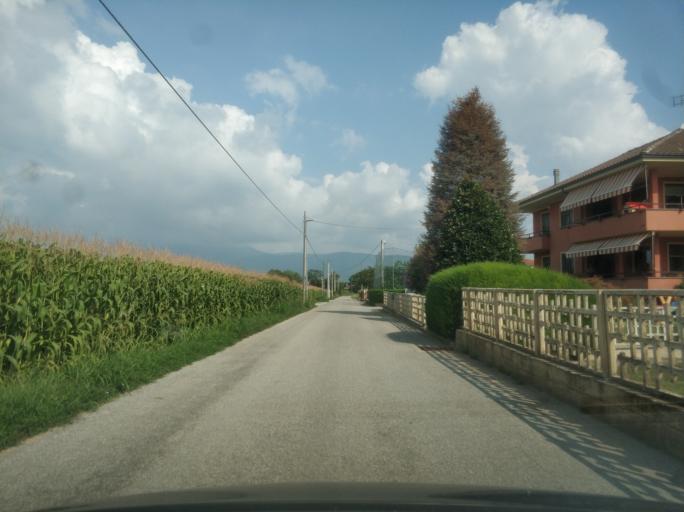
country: IT
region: Piedmont
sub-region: Provincia di Cuneo
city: Caraglio
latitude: 44.4336
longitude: 7.4321
